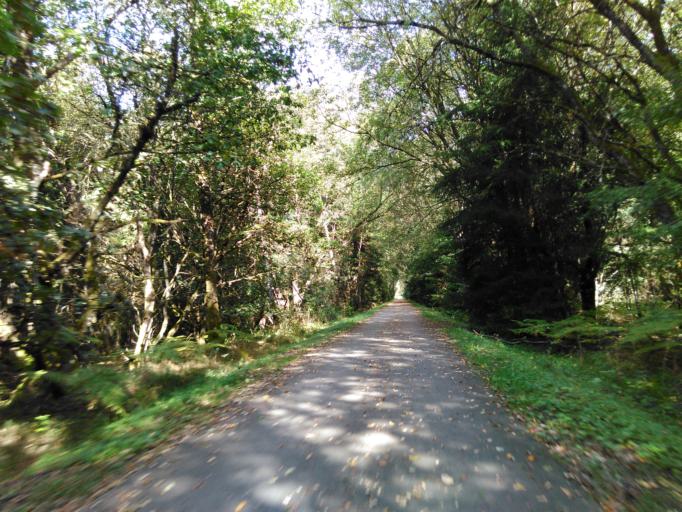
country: BE
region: Wallonia
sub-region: Province du Luxembourg
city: Gouvy
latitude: 50.1279
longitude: 5.9100
